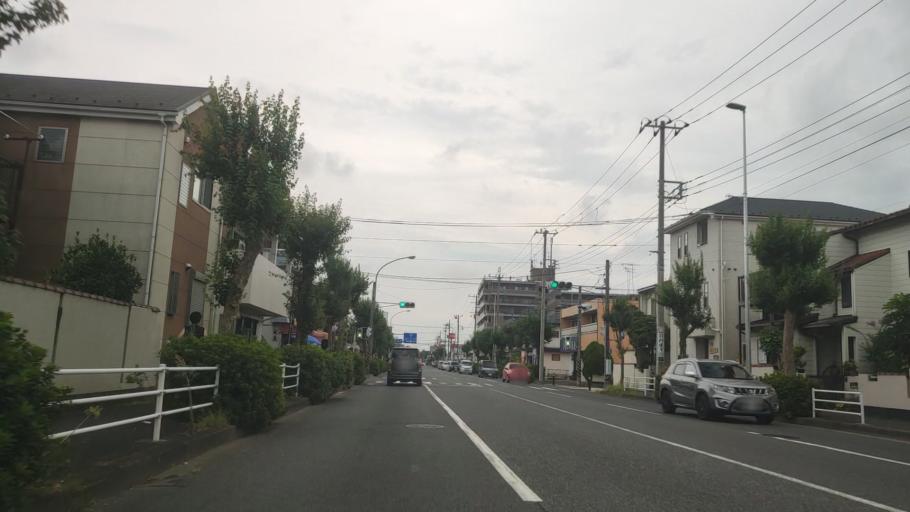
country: JP
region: Kanagawa
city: Minami-rinkan
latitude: 35.4447
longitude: 139.4843
